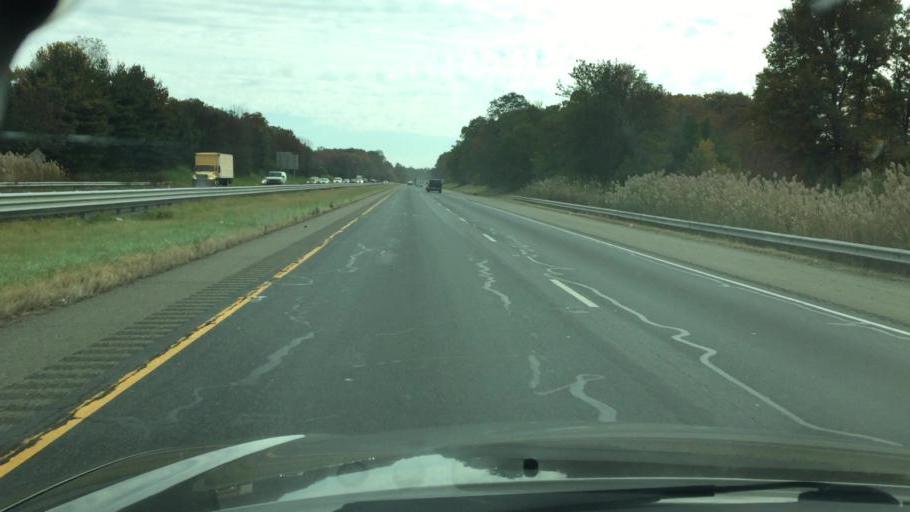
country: US
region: New Jersey
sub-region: Morris County
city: Madison
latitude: 40.7808
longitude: -74.4137
